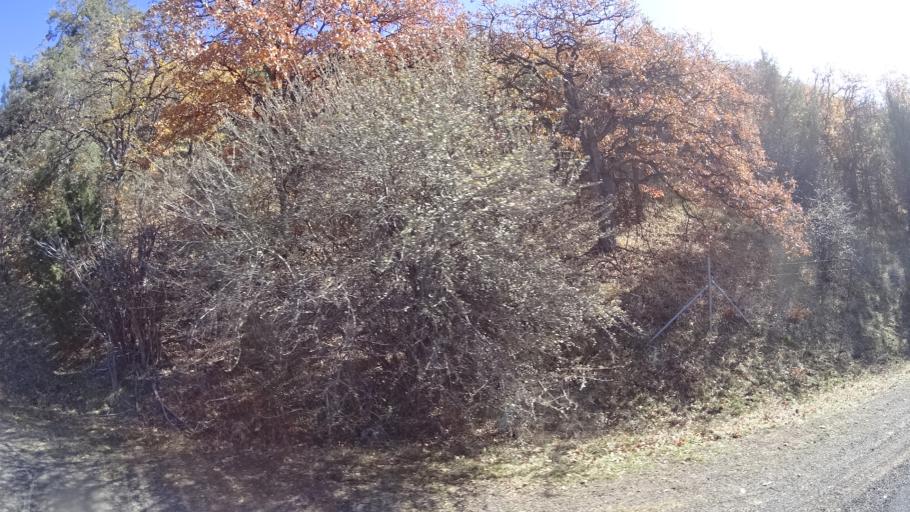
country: US
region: California
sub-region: Siskiyou County
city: Montague
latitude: 41.8289
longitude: -122.3329
